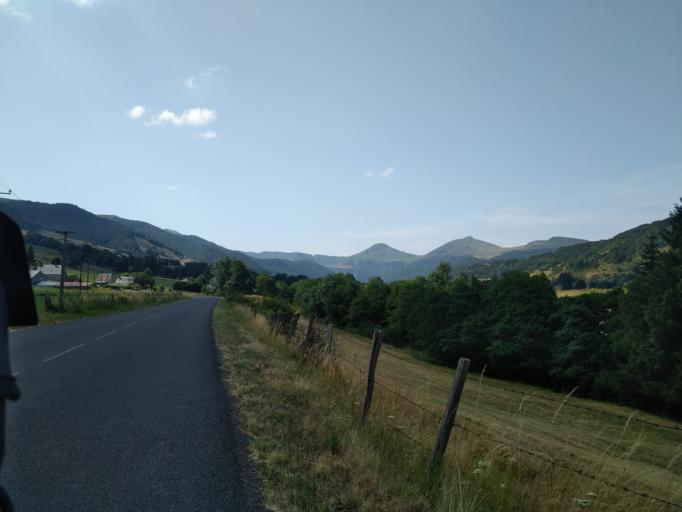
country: FR
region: Auvergne
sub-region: Departement du Cantal
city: Riom-es-Montagnes
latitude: 45.1703
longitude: 2.7141
